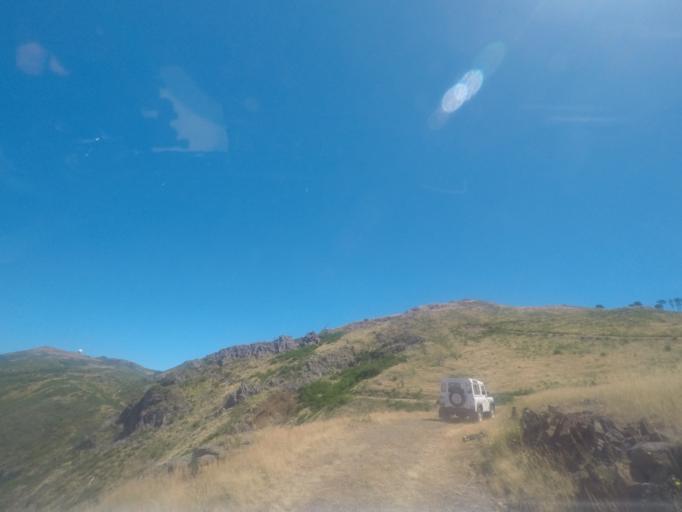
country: PT
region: Madeira
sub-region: Funchal
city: Nossa Senhora do Monte
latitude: 32.7086
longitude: -16.9161
